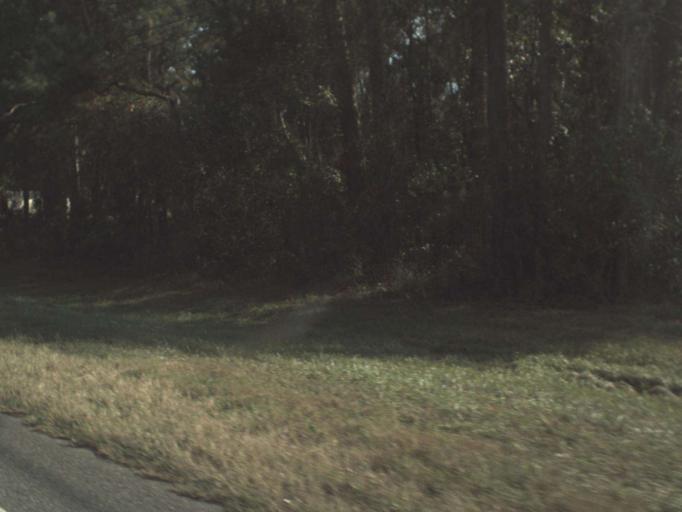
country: US
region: Florida
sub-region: Gadsden County
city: Midway
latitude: 30.4686
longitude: -84.4013
